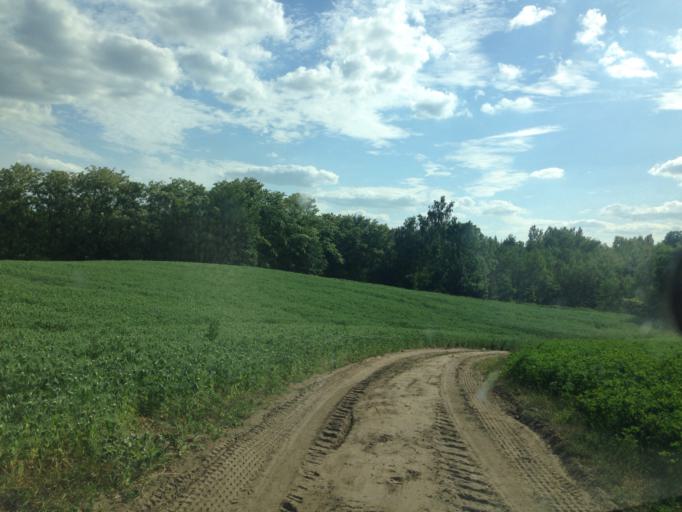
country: PL
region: Kujawsko-Pomorskie
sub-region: Powiat brodnicki
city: Brzozie
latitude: 53.3134
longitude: 19.5694
